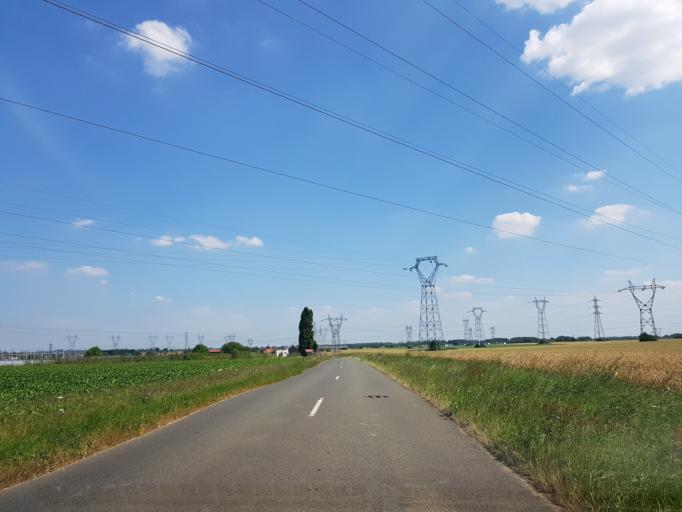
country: FR
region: Nord-Pas-de-Calais
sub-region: Departement du Nord
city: Abscon
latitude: 50.3206
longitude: 3.3204
